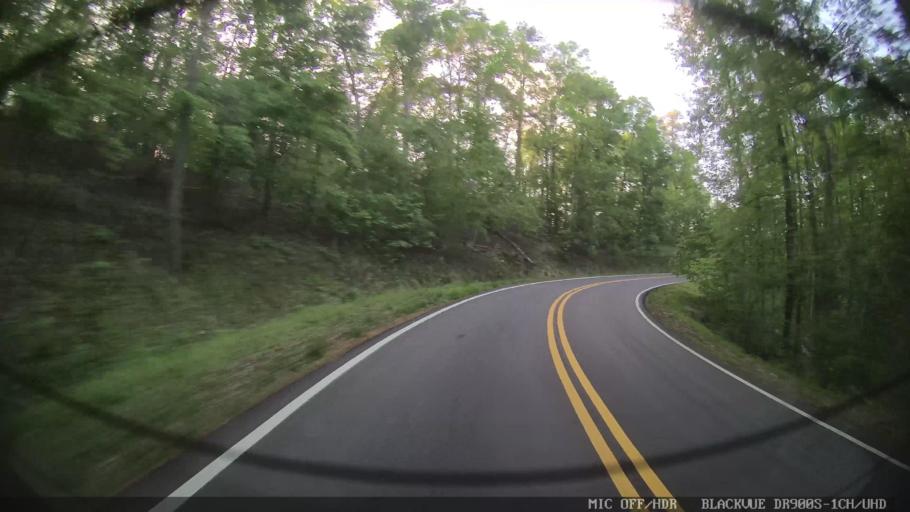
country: US
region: Georgia
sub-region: Bartow County
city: Emerson
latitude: 34.0888
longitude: -84.7666
